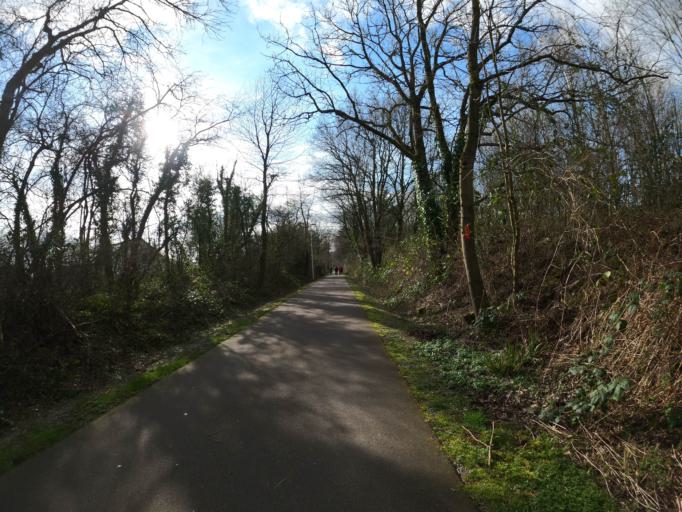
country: DE
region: North Rhine-Westphalia
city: Haan
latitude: 51.2090
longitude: 7.0526
